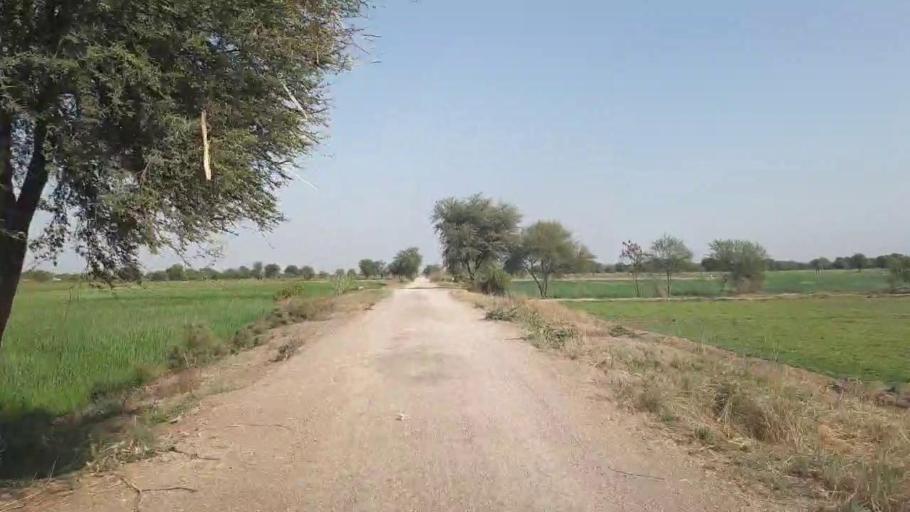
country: PK
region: Sindh
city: Dhoro Naro
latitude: 25.4420
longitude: 69.5294
